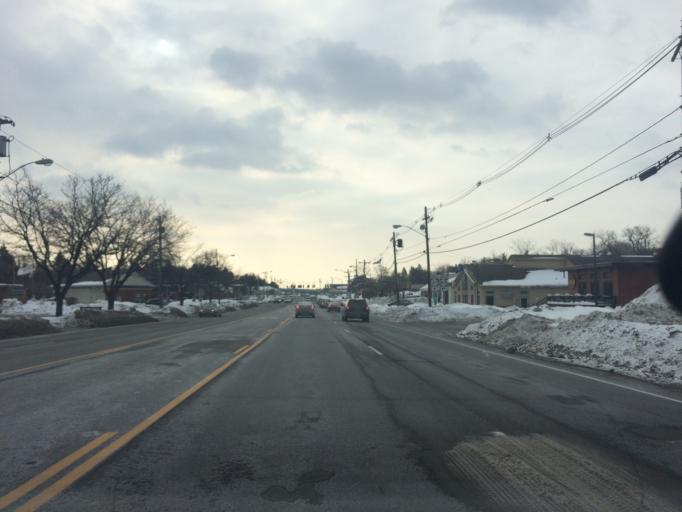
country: US
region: New York
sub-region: Monroe County
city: Brighton
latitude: 43.1123
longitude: -77.5494
